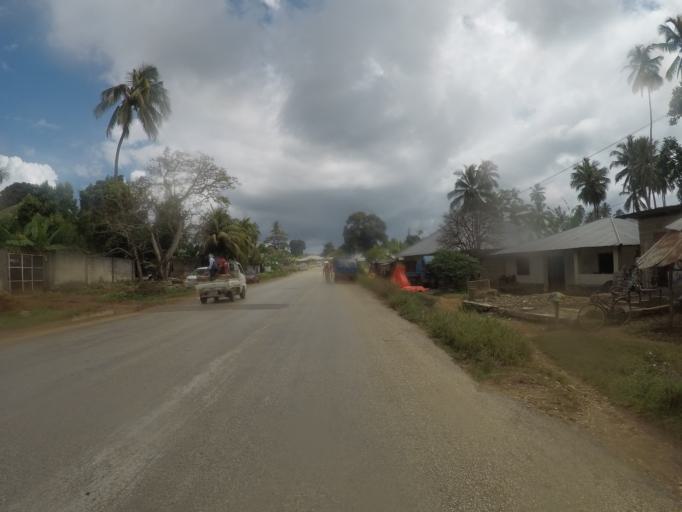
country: TZ
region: Zanzibar Central/South
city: Koani
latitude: -6.0508
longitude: 39.2258
